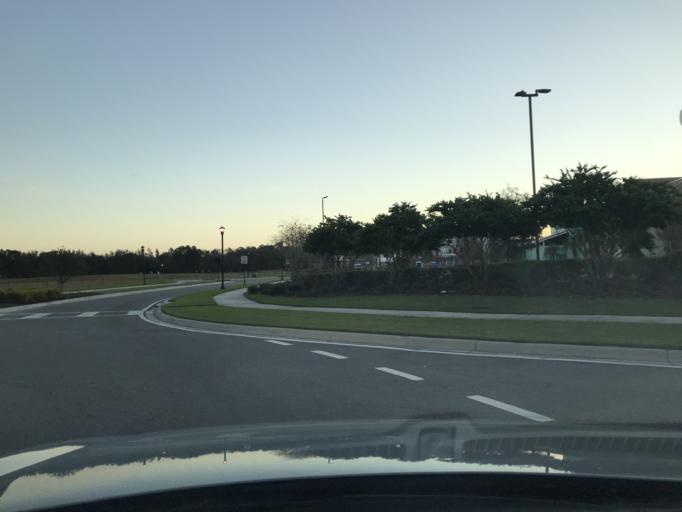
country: US
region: Florida
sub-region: Hillsborough County
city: Pebble Creek
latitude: 28.1960
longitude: -82.3906
